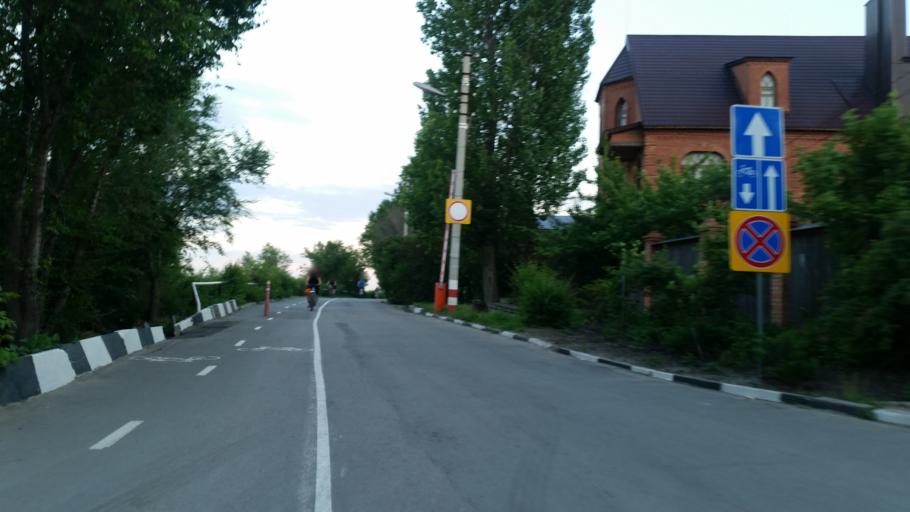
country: RU
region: Ulyanovsk
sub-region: Ulyanovskiy Rayon
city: Ulyanovsk
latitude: 54.3243
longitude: 48.4095
